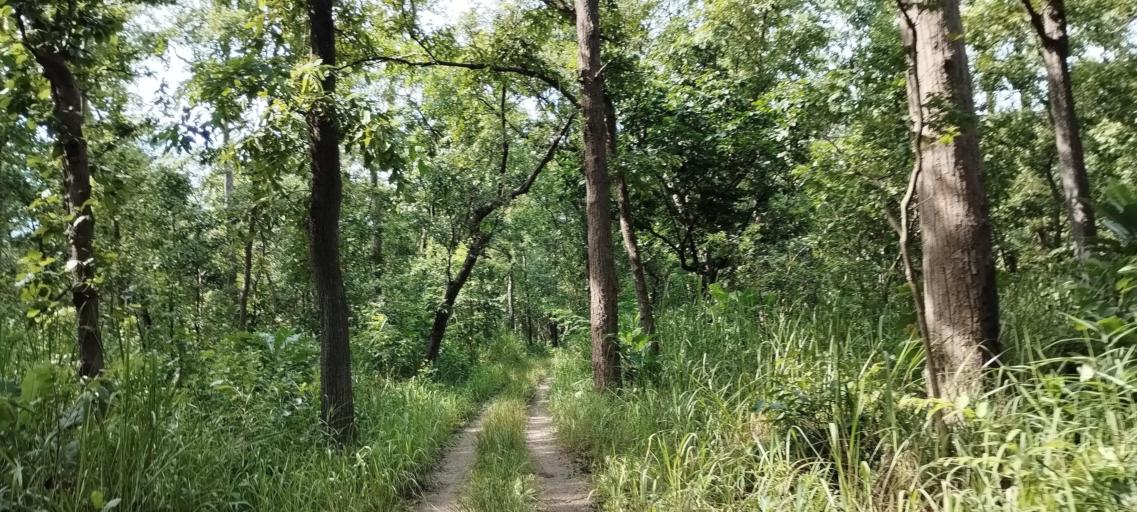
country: NP
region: Far Western
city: Tikapur
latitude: 28.5670
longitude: 81.2921
